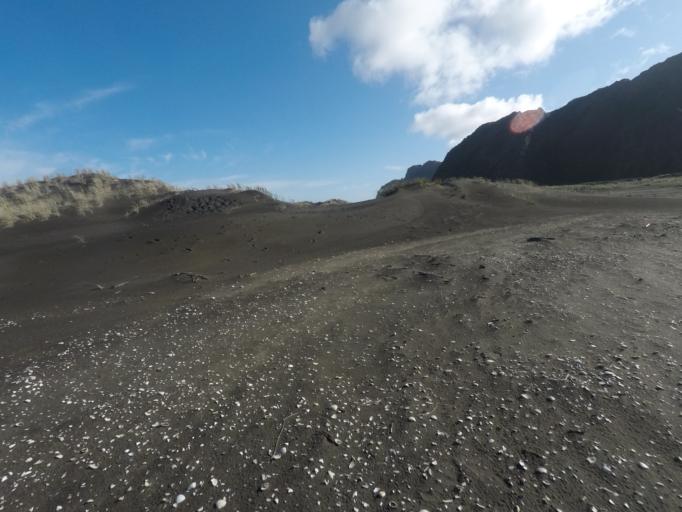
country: NZ
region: Auckland
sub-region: Auckland
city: Muriwai Beach
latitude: -36.9974
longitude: 174.4748
